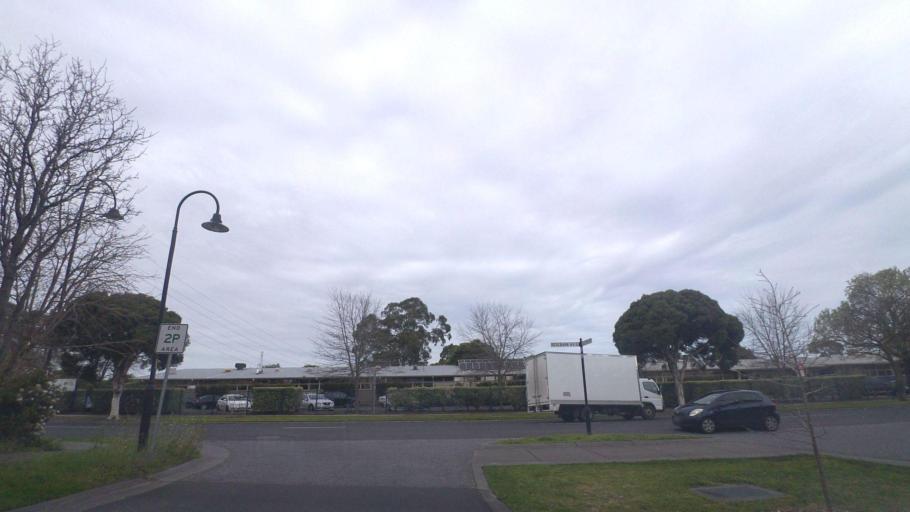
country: AU
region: Victoria
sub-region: Greater Dandenong
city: Springvale
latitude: -37.9400
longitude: 145.1372
